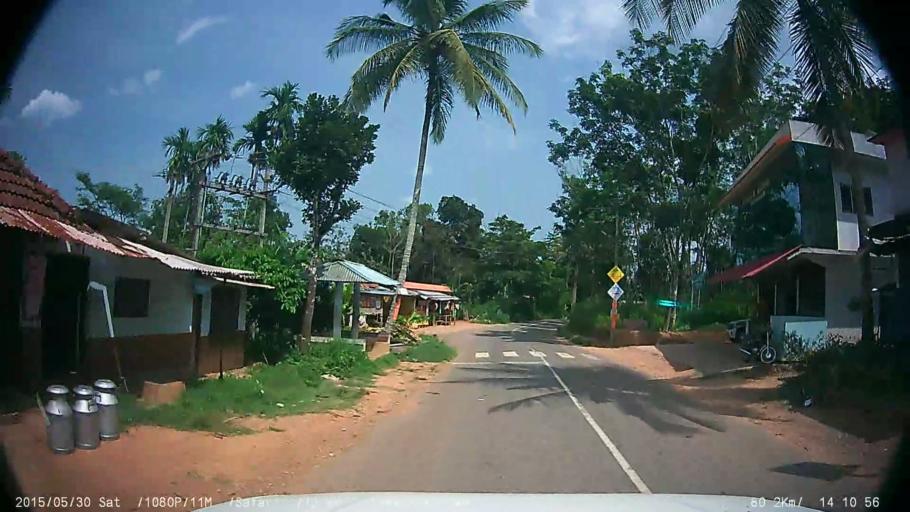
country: IN
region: Kerala
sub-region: Wayanad
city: Panamaram
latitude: 11.7955
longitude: 76.0526
